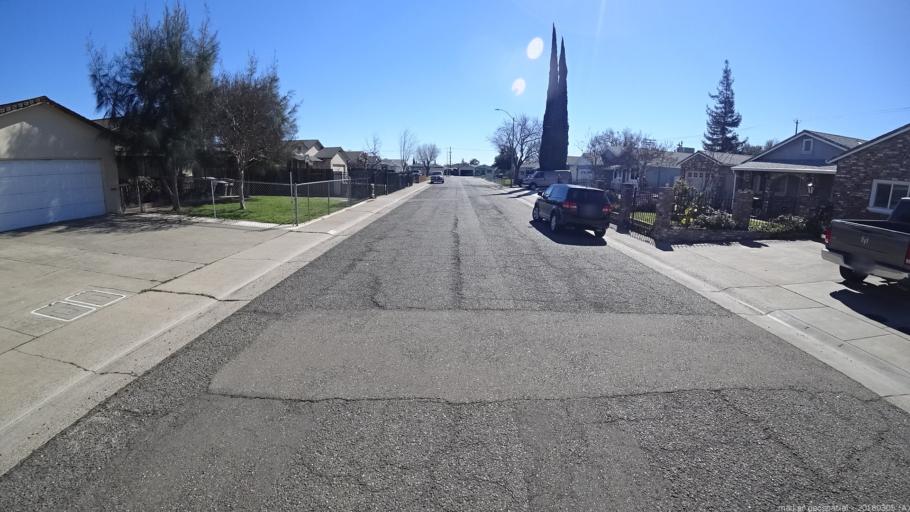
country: US
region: California
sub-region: Sacramento County
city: Florin
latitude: 38.4904
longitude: -121.3898
